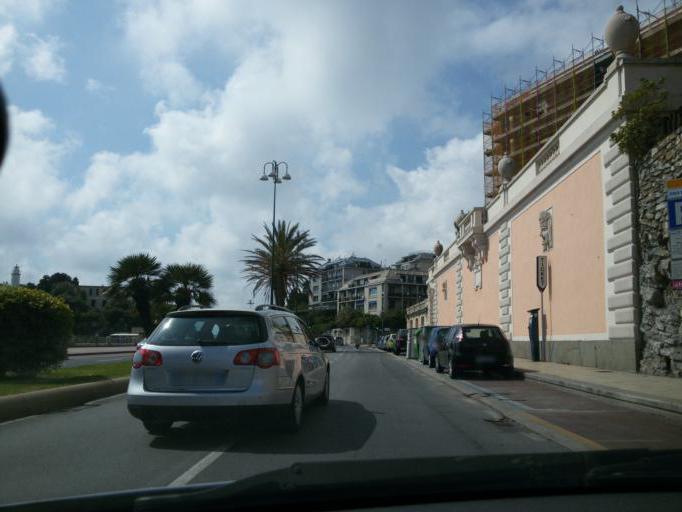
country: IT
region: Liguria
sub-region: Provincia di Genova
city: San Teodoro
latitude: 44.3919
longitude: 8.9553
